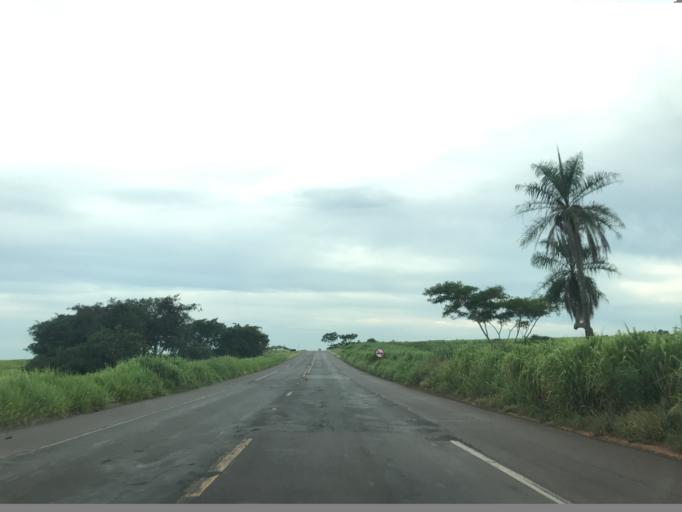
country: BR
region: Sao Paulo
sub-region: Tupa
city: Tupa
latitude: -21.6652
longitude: -50.5601
